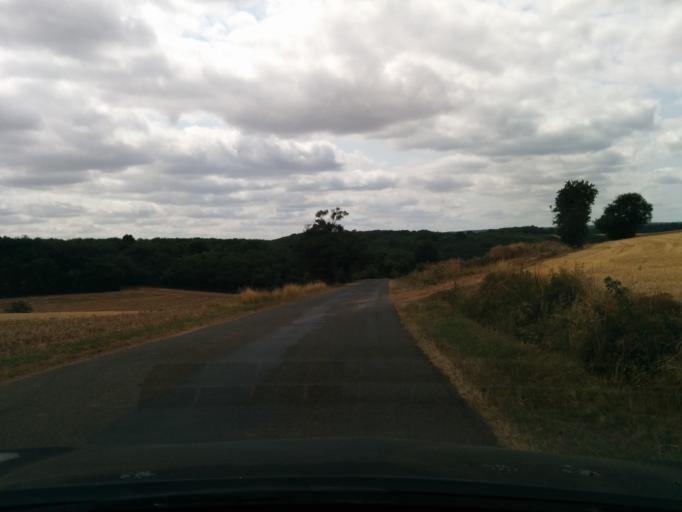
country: FR
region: Centre
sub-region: Departement du Cher
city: Sancerre
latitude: 47.3253
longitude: 2.7652
